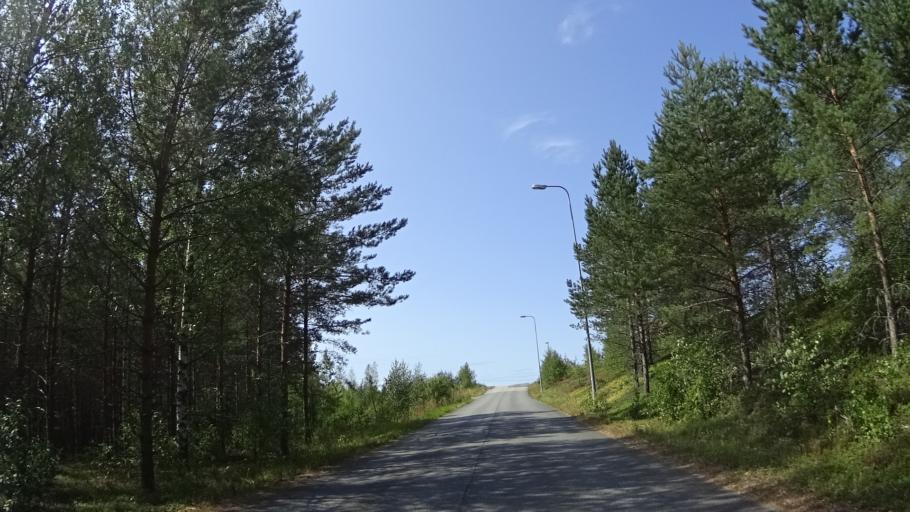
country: FI
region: Pirkanmaa
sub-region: Ylae-Pirkanmaa
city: Maenttae
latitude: 61.8589
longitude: 24.8214
